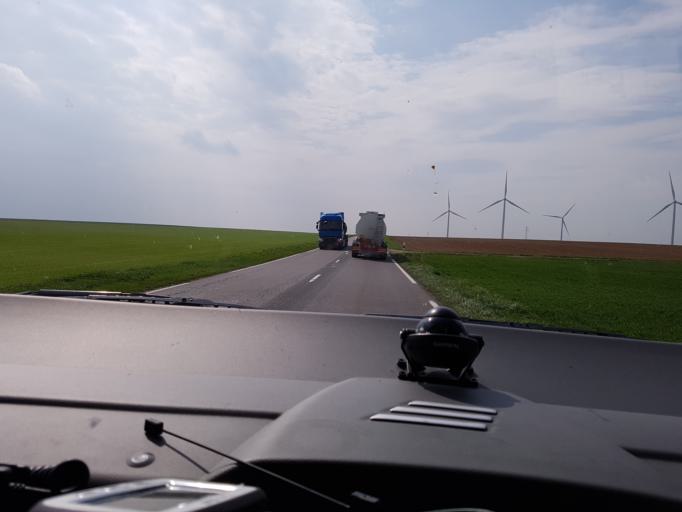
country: FR
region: Picardie
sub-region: Departement de l'Aisne
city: Crouy
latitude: 49.4318
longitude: 3.3526
